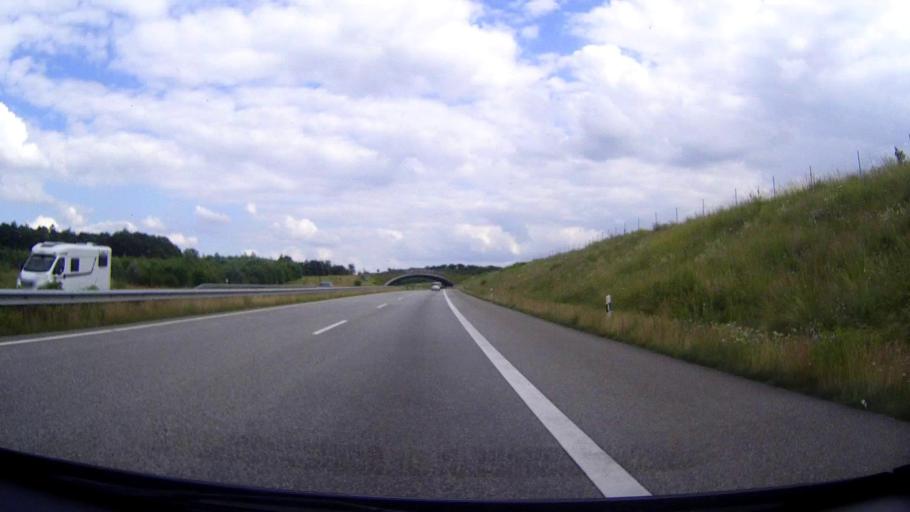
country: DE
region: Schleswig-Holstein
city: Strukdorf
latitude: 53.9207
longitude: 10.4968
